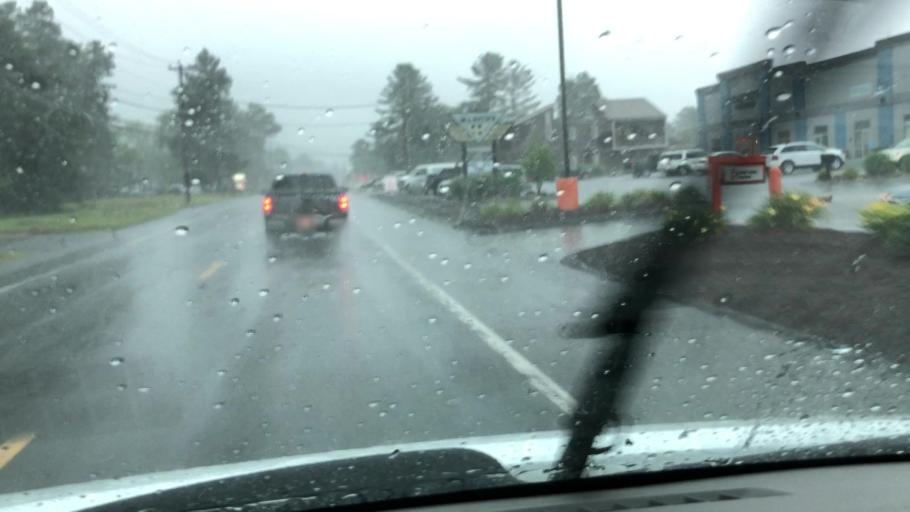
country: US
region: Massachusetts
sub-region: Hampden County
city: Westfield
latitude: 42.1560
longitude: -72.7258
